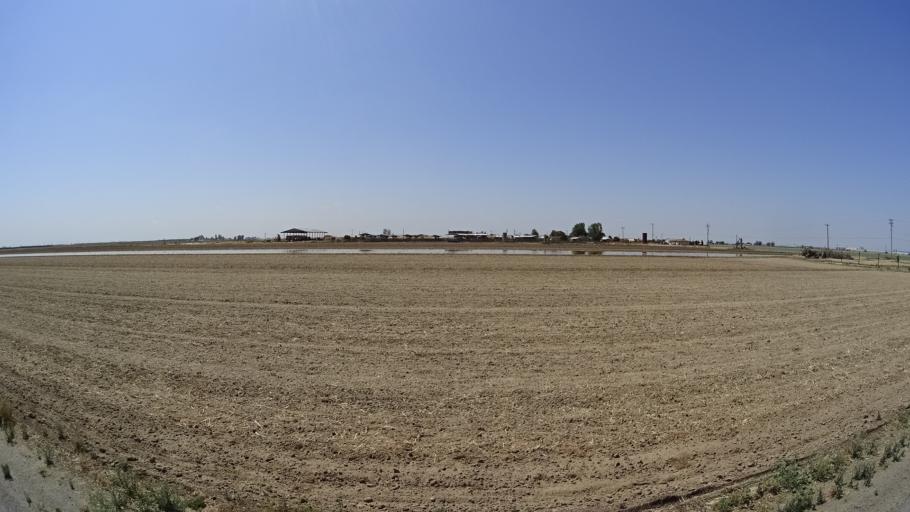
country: US
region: California
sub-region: Kings County
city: Home Garden
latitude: 36.2839
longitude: -119.6176
